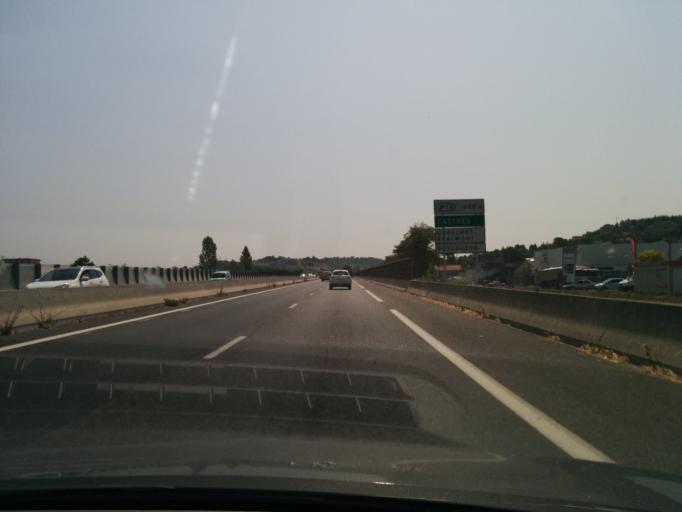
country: FR
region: Midi-Pyrenees
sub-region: Departement du Tarn
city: Le Sequestre
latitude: 43.9128
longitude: 2.1268
